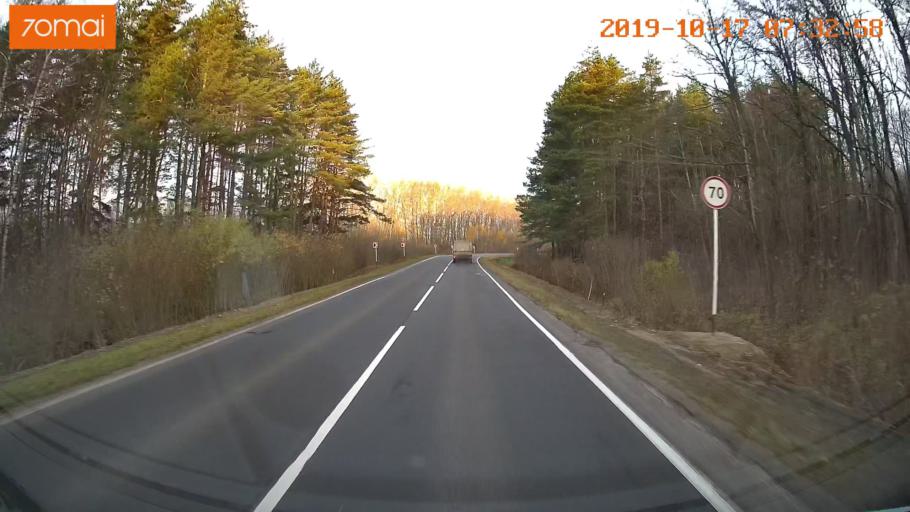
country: RU
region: Ivanovo
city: Gavrilov Posad
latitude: 56.4011
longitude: 39.9637
